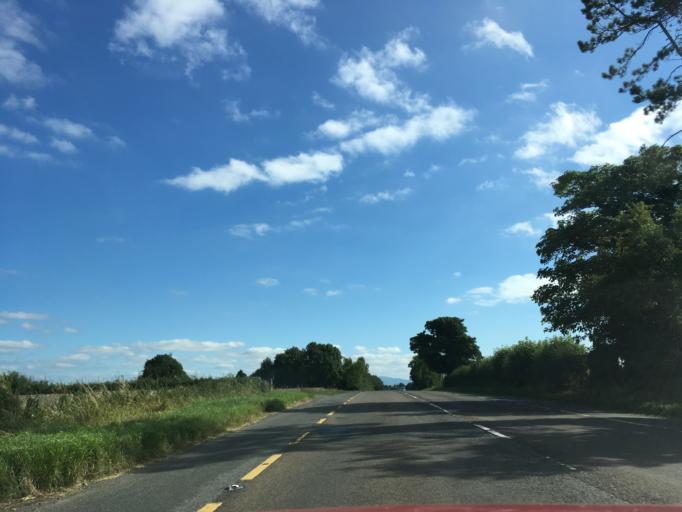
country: IE
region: Munster
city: Cashel
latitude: 52.4931
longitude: -7.8899
